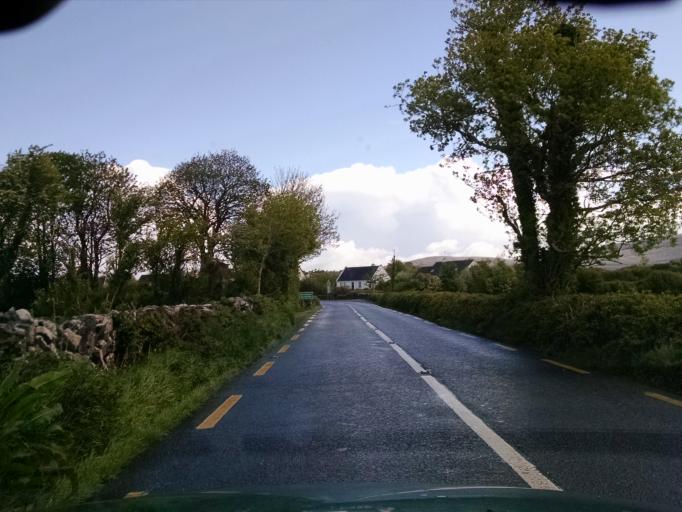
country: IE
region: Connaught
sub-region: County Galway
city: Bearna
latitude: 53.1106
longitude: -9.1523
